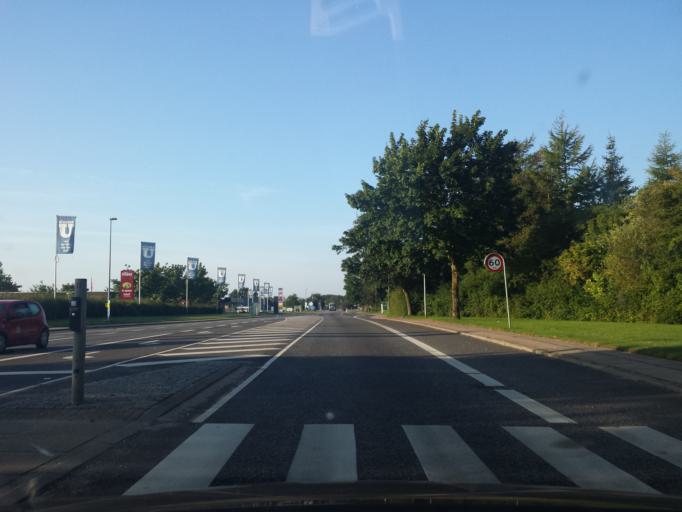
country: DK
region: South Denmark
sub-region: Sonderborg Kommune
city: Grasten
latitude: 54.9124
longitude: 9.5877
